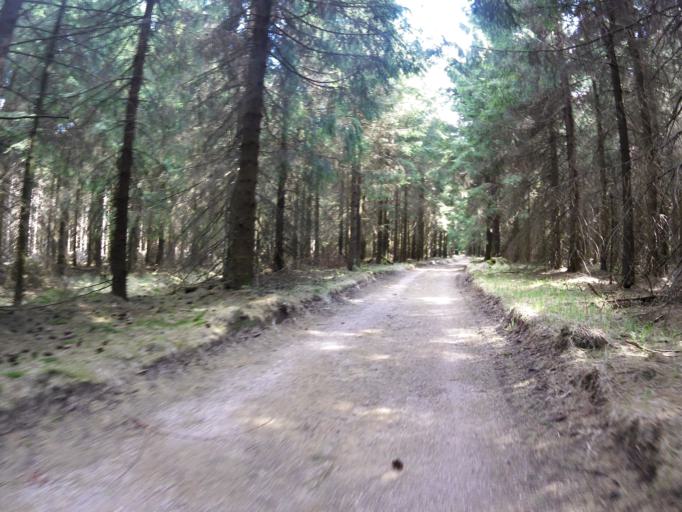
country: DE
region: Thuringia
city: Unterschonau
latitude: 50.7454
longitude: 10.5735
